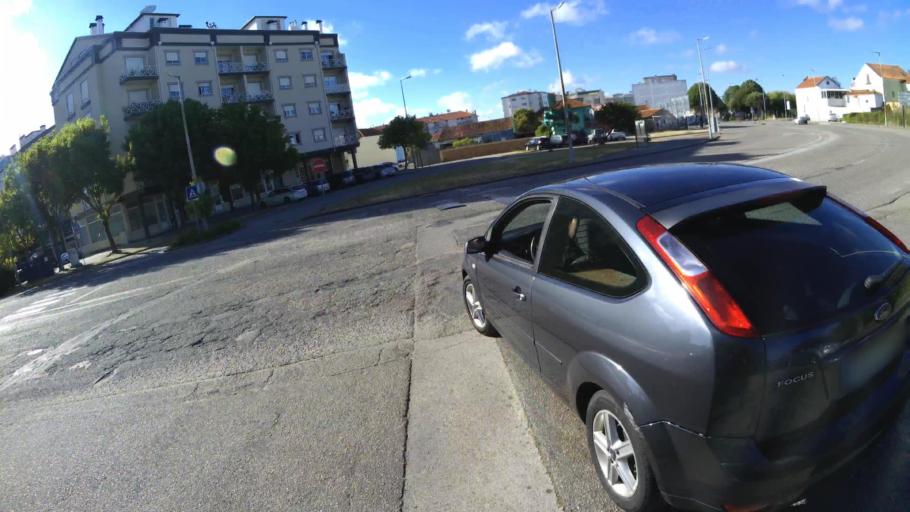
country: PT
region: Aveiro
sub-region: Aveiro
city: Aveiro
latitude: 40.6463
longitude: -8.6354
